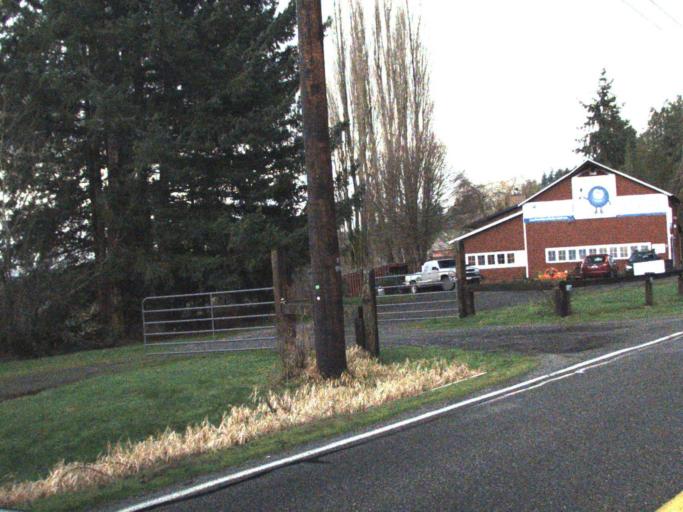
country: US
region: Washington
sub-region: Snohomish County
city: Silver Firs
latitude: 47.8819
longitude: -122.1298
